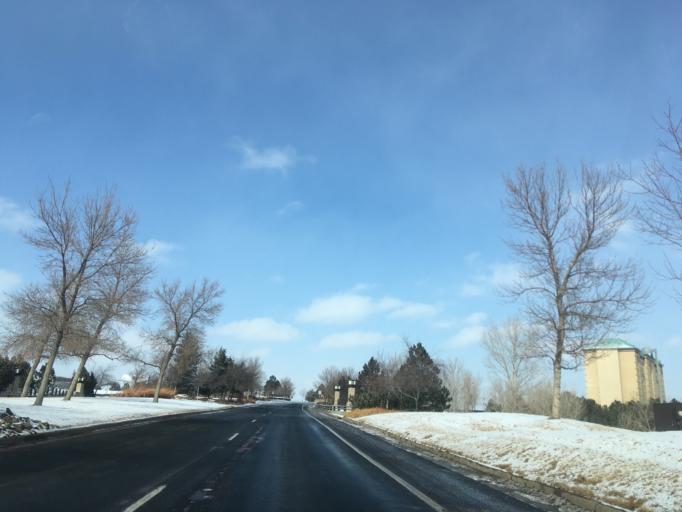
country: US
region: Colorado
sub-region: Broomfield County
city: Broomfield
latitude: 39.9250
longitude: -105.1208
